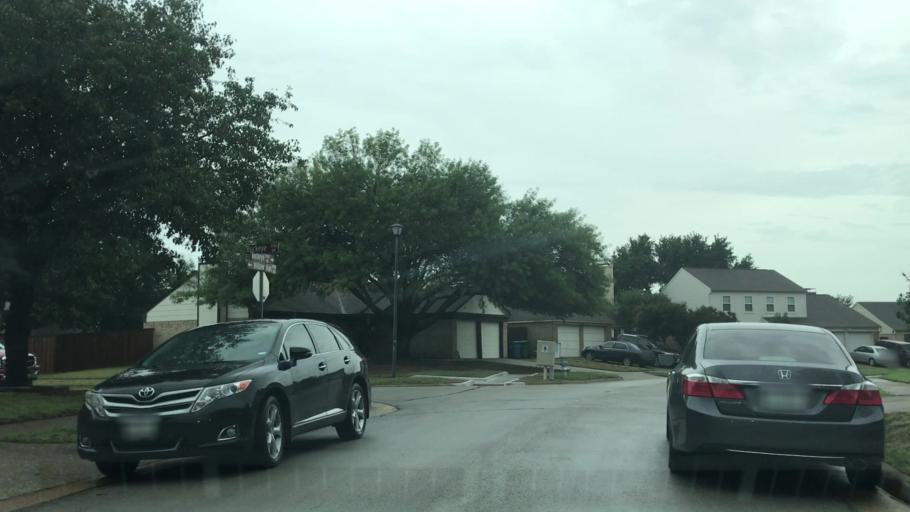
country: US
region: Texas
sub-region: Denton County
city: Flower Mound
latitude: 33.0399
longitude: -97.0548
